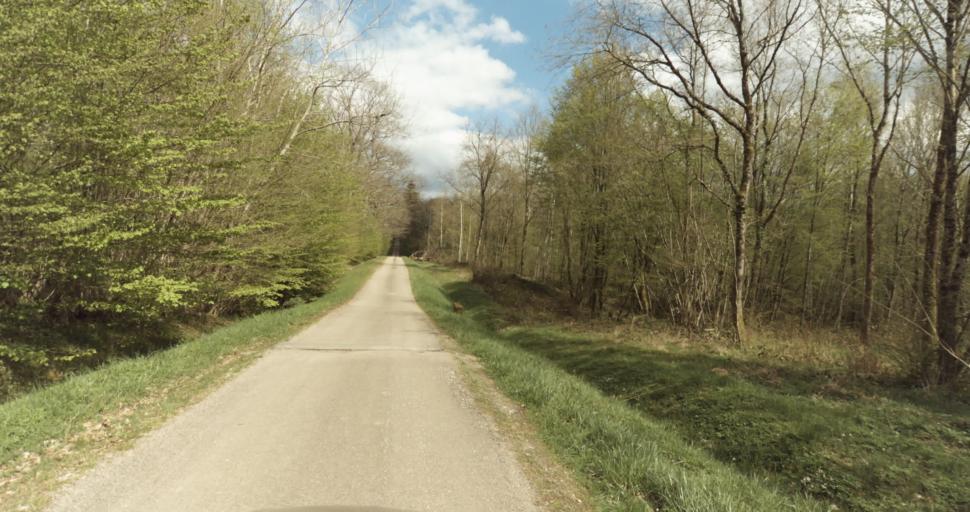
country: FR
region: Franche-Comte
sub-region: Departement du Jura
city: Champvans
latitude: 47.1591
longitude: 5.4379
